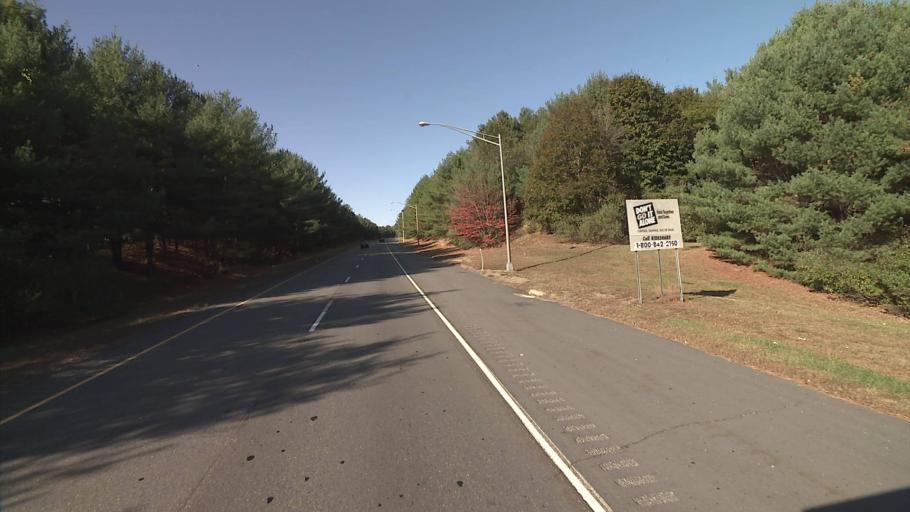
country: US
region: Connecticut
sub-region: Windham County
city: Willimantic
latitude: 41.7313
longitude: -72.2027
